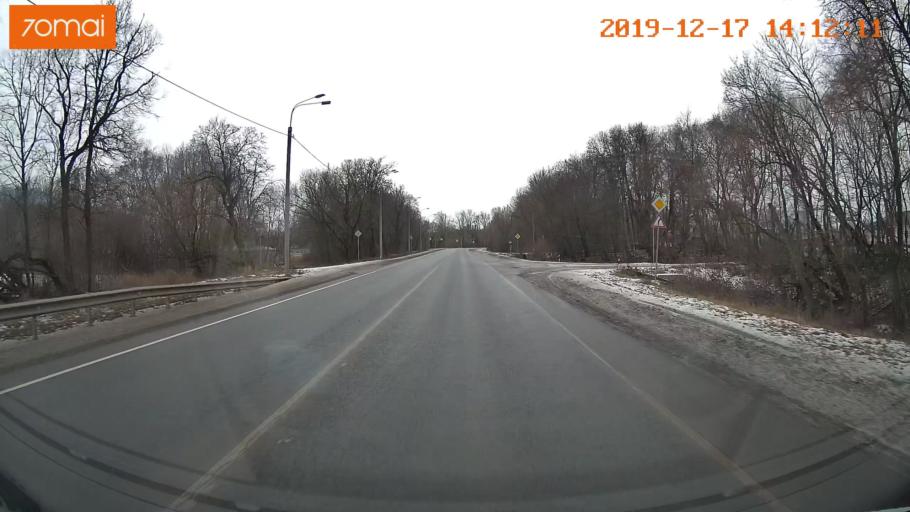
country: RU
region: Rjazan
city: Rybnoye
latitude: 54.5263
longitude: 39.5066
